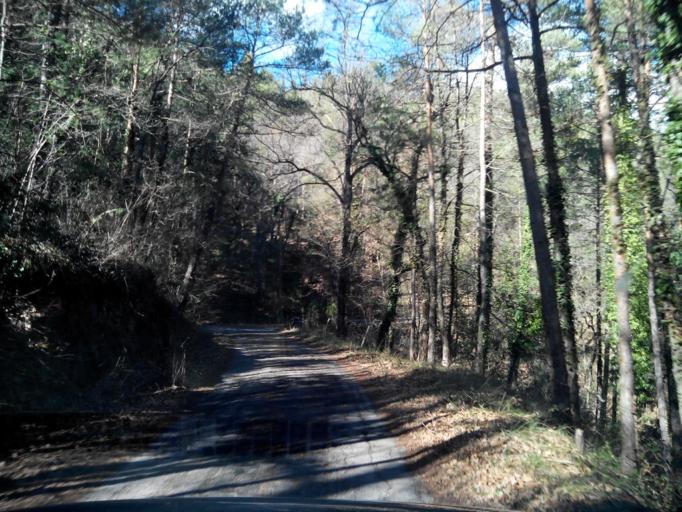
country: ES
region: Catalonia
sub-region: Provincia de Barcelona
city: Vilada
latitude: 42.1328
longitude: 1.9273
